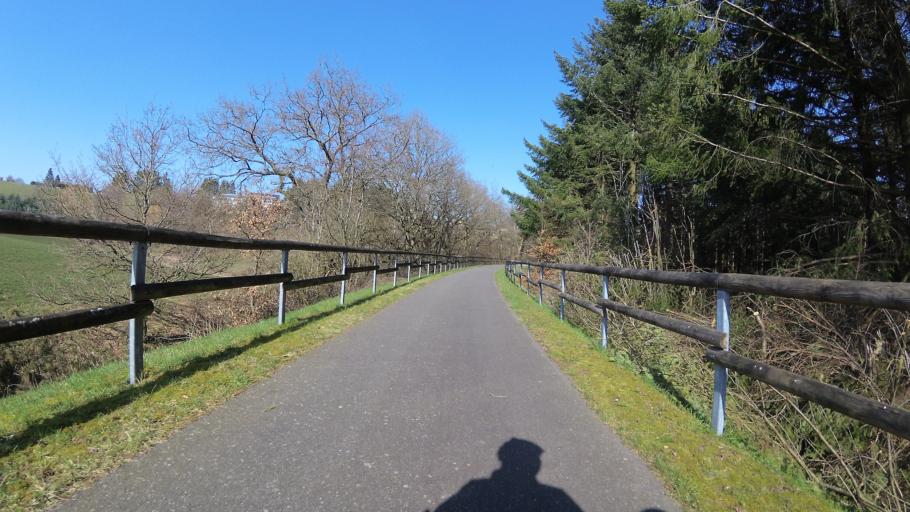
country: DE
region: Rheinland-Pfalz
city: Reinsfeld
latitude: 49.6690
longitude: 6.8713
